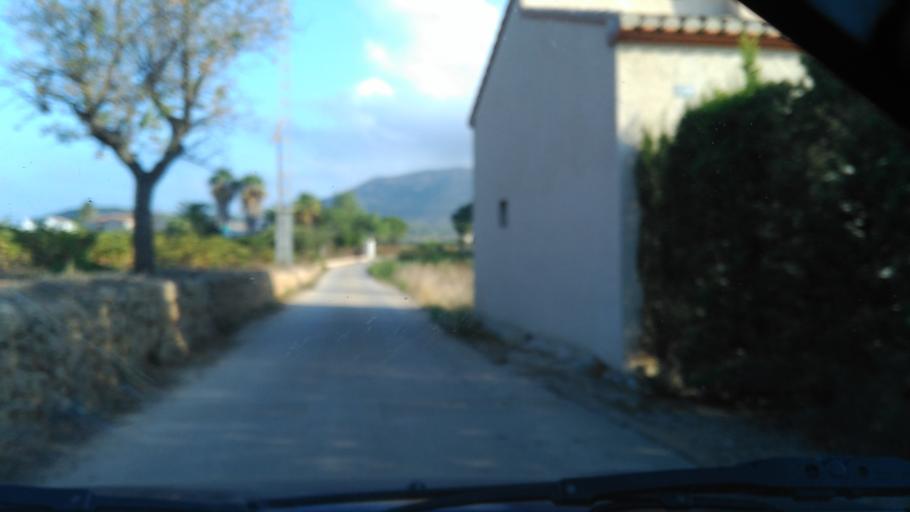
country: ES
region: Valencia
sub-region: Provincia de Alicante
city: Gata de Gorgos
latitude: 38.7852
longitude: 0.0893
